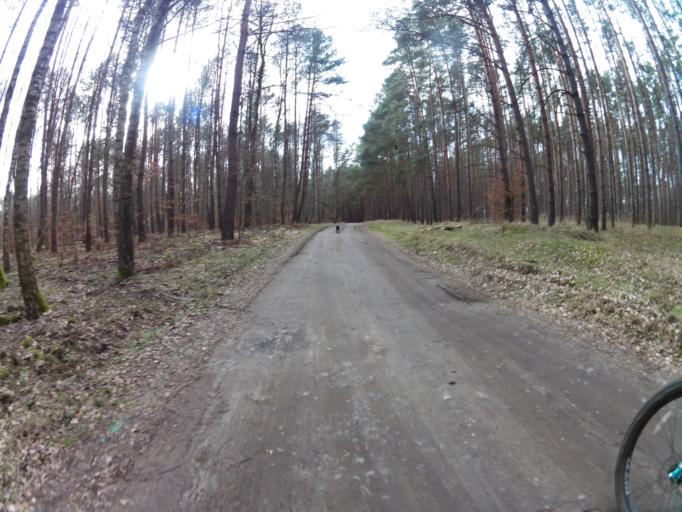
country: PL
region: Lubusz
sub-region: Powiat gorzowski
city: Lubiszyn
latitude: 52.7720
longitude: 14.8417
